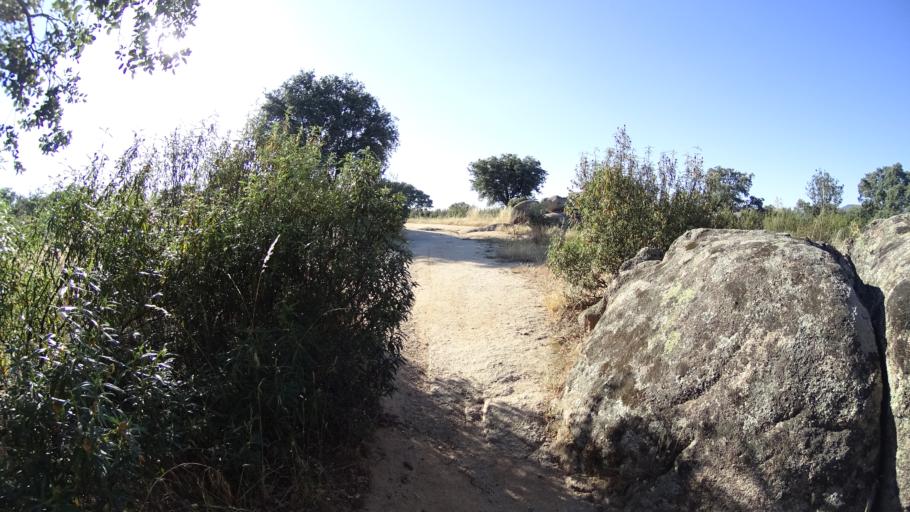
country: ES
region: Madrid
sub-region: Provincia de Madrid
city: Galapagar
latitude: 40.5911
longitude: -3.9756
